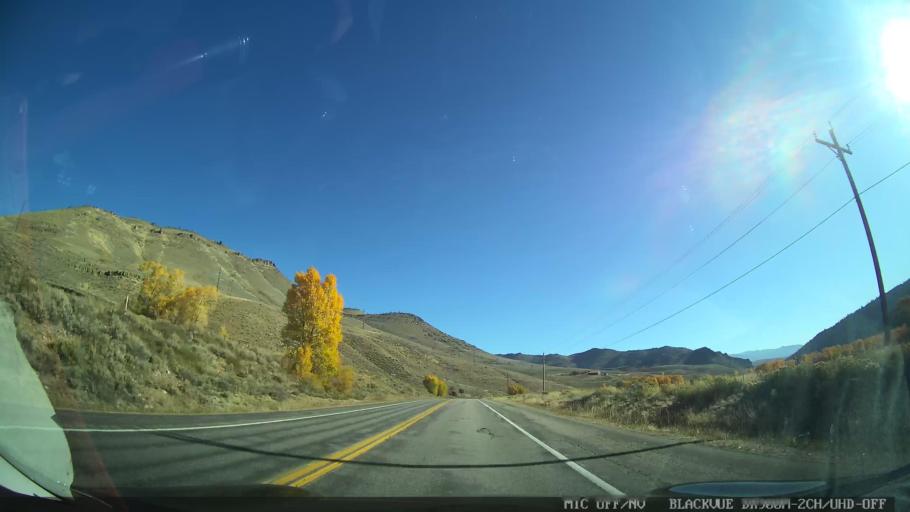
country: US
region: Colorado
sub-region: Grand County
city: Hot Sulphur Springs
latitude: 40.1049
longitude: -106.0260
